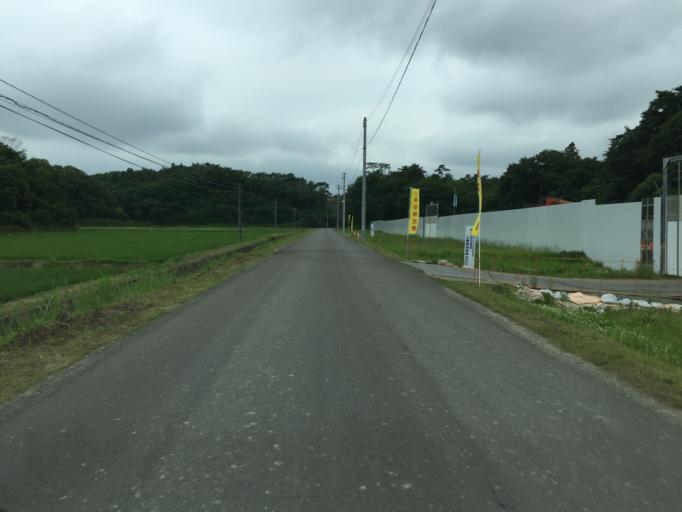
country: JP
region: Fukushima
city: Namie
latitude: 37.7288
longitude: 140.9573
